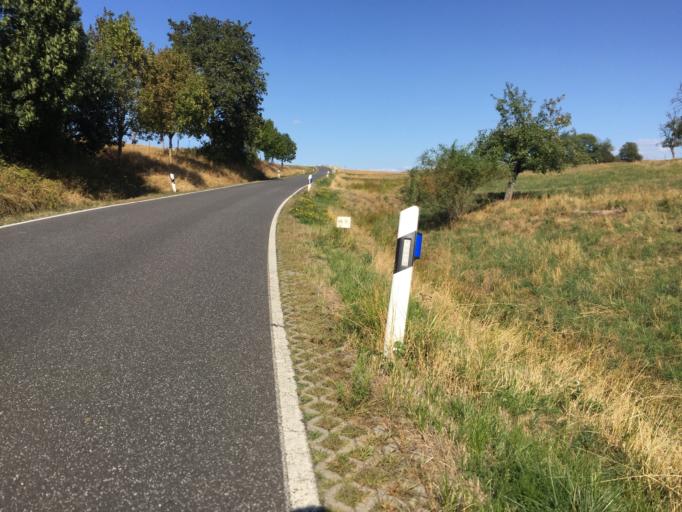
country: DE
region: Hesse
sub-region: Regierungsbezirk Giessen
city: Grunberg
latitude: 50.6045
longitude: 8.9260
